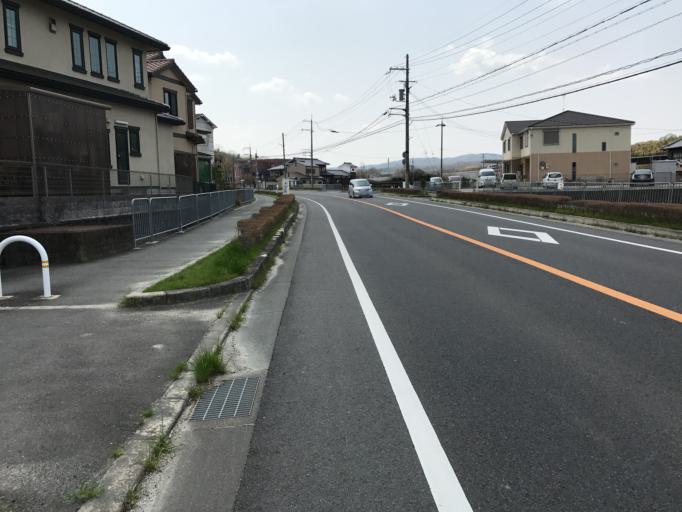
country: JP
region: Kyoto
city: Tanabe
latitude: 34.7783
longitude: 135.7851
